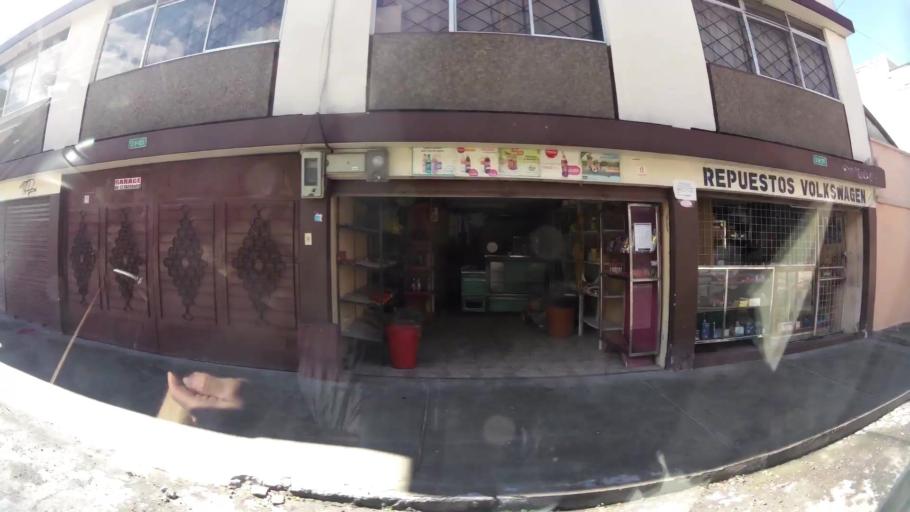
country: EC
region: Pichincha
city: Quito
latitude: -0.2403
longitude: -78.5289
